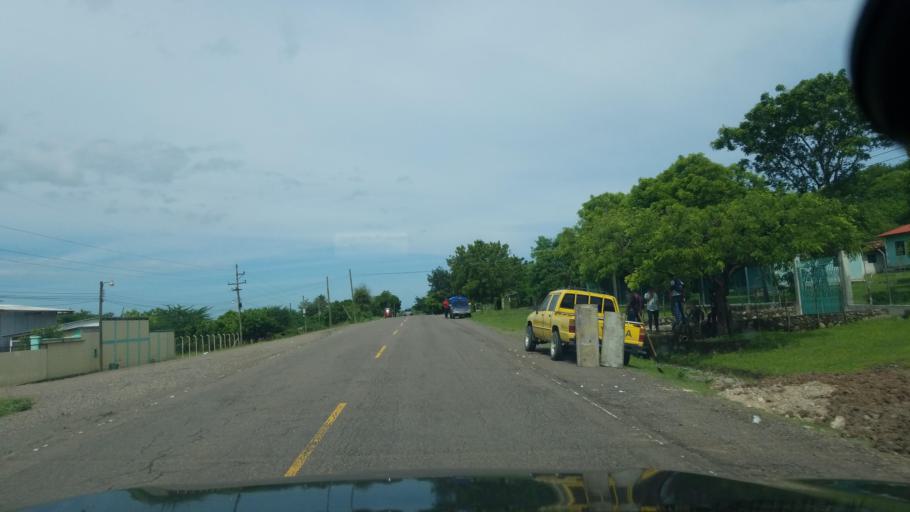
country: HN
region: Choluteca
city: Santa Ana de Yusguare
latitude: 13.3591
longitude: -87.0948
